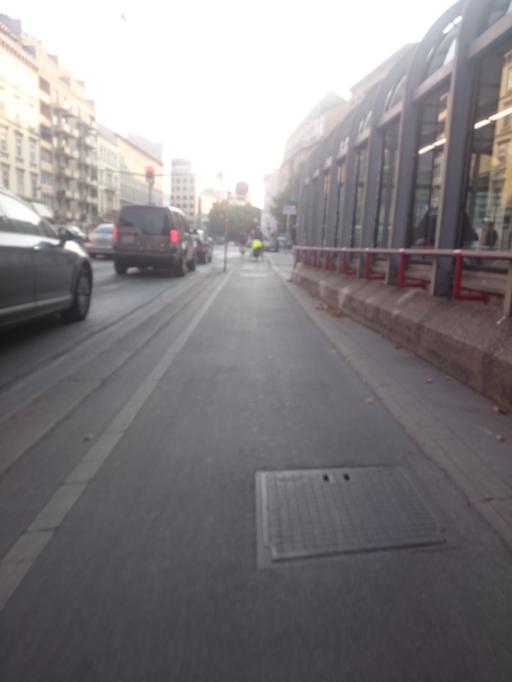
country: AT
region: Vienna
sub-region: Wien Stadt
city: Vienna
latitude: 48.2150
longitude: 16.3848
